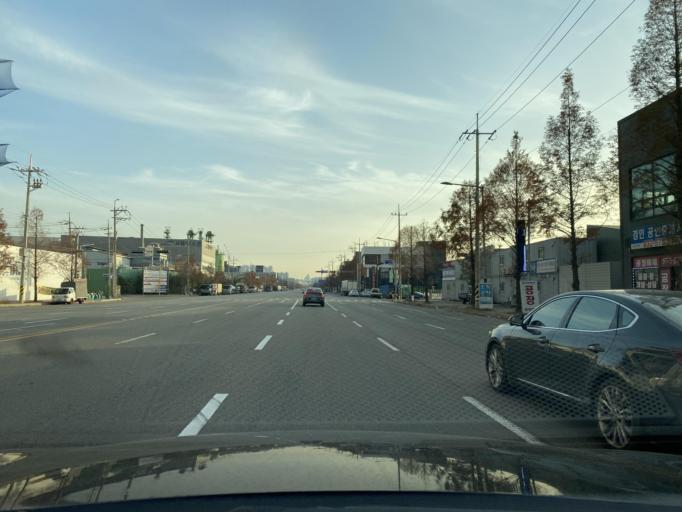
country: KR
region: Incheon
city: Incheon
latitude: 37.5045
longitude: 126.6617
